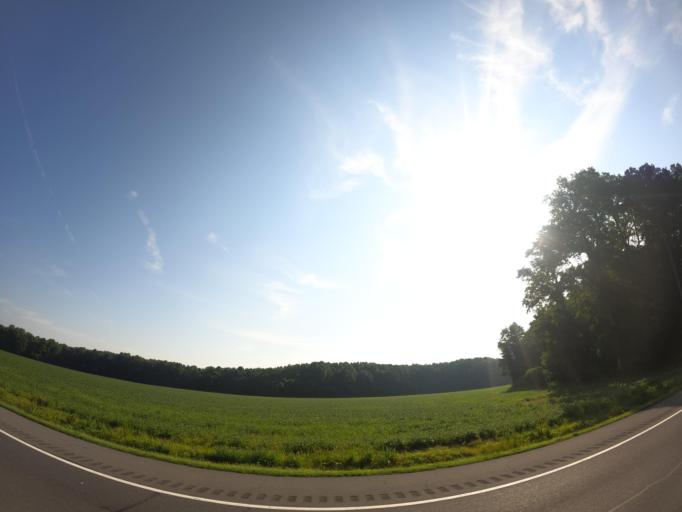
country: US
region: Delaware
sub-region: Sussex County
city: Millsboro
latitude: 38.6100
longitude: -75.3287
